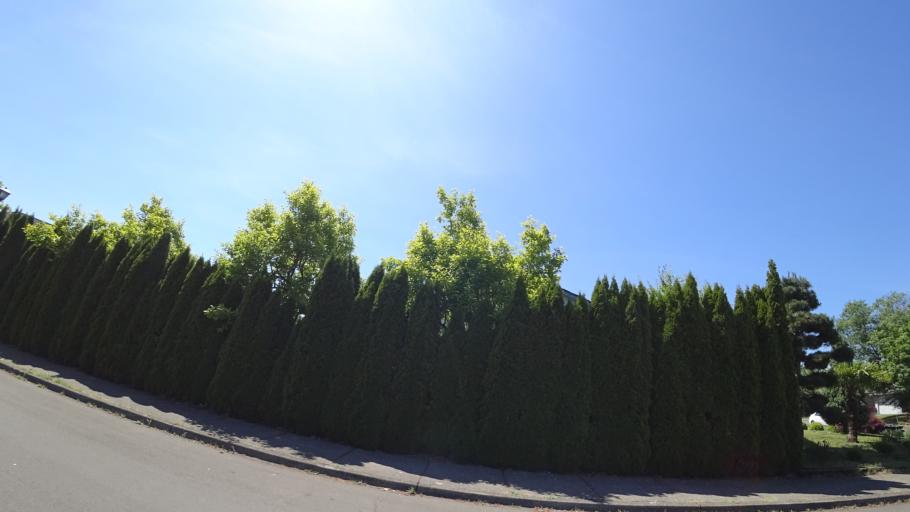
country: US
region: Oregon
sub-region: Washington County
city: Tigard
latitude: 45.4411
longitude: -122.8060
